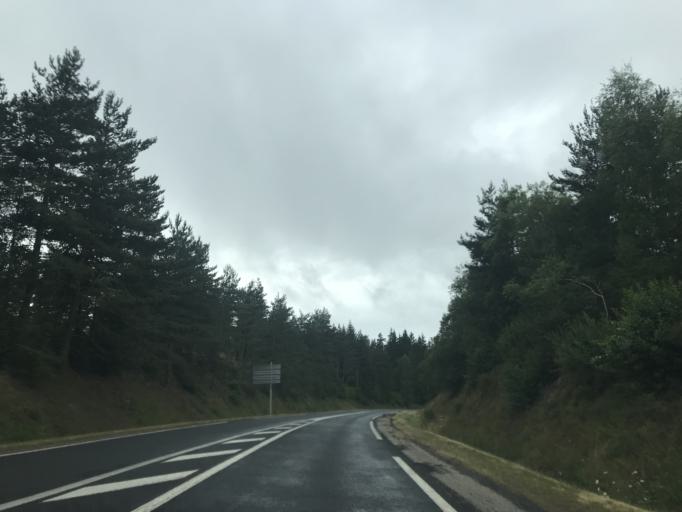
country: FR
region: Auvergne
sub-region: Departement de la Haute-Loire
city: Fontannes
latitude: 45.2449
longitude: 3.7672
